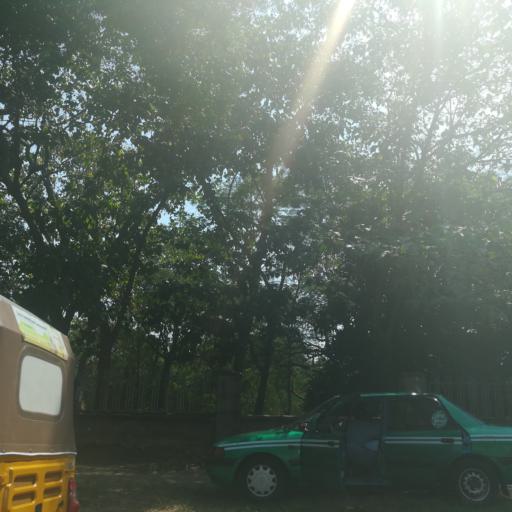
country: NG
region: Abuja Federal Capital Territory
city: Abuja
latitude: 9.0720
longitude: 7.4365
